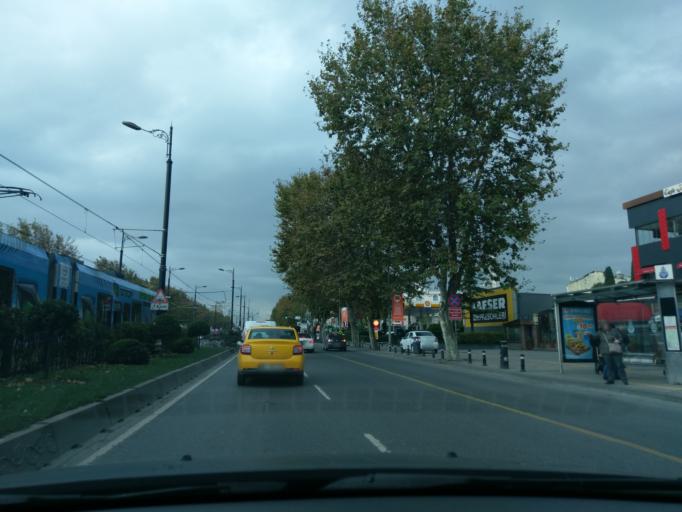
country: TR
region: Istanbul
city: Istanbul
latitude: 41.0174
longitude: 28.9292
